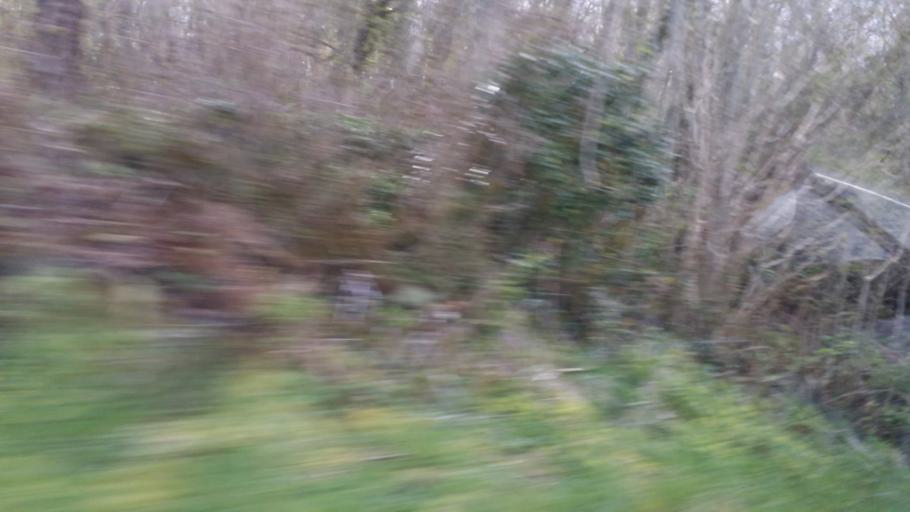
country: GB
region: Northern Ireland
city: Irvinestown
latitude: 54.4720
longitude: -7.8687
